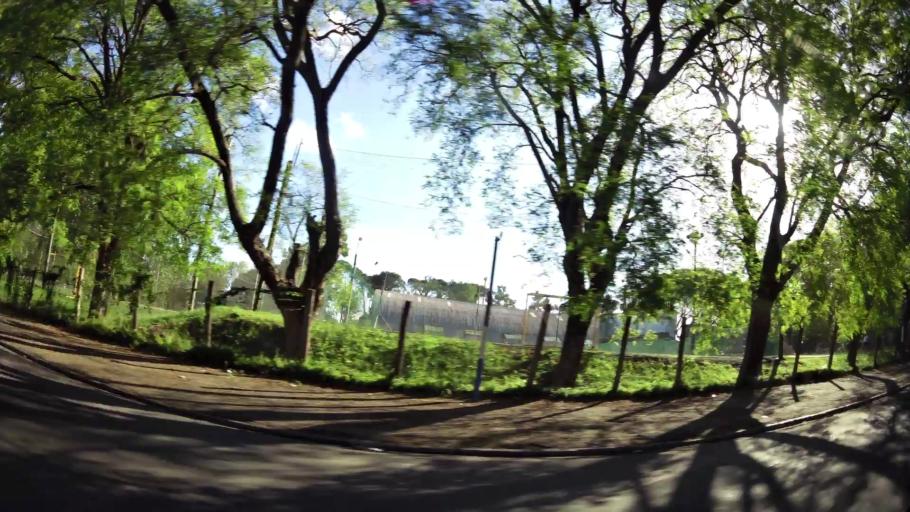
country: UY
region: Montevideo
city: Montevideo
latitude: -34.8535
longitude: -56.2081
